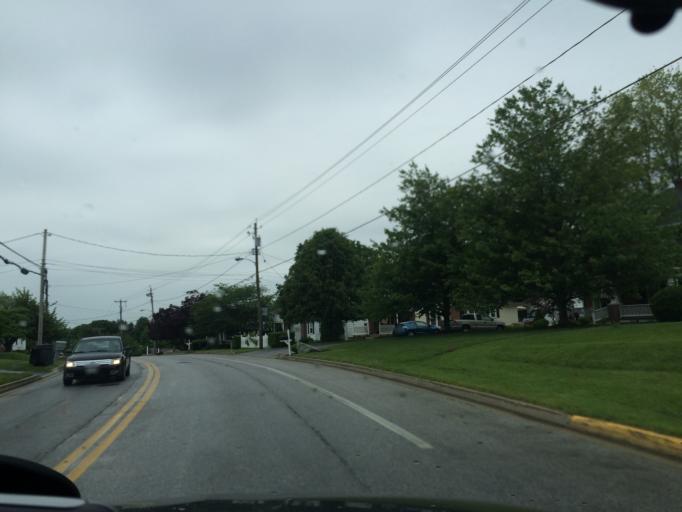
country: US
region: Maryland
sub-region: Carroll County
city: Westminster
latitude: 39.5831
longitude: -77.0147
